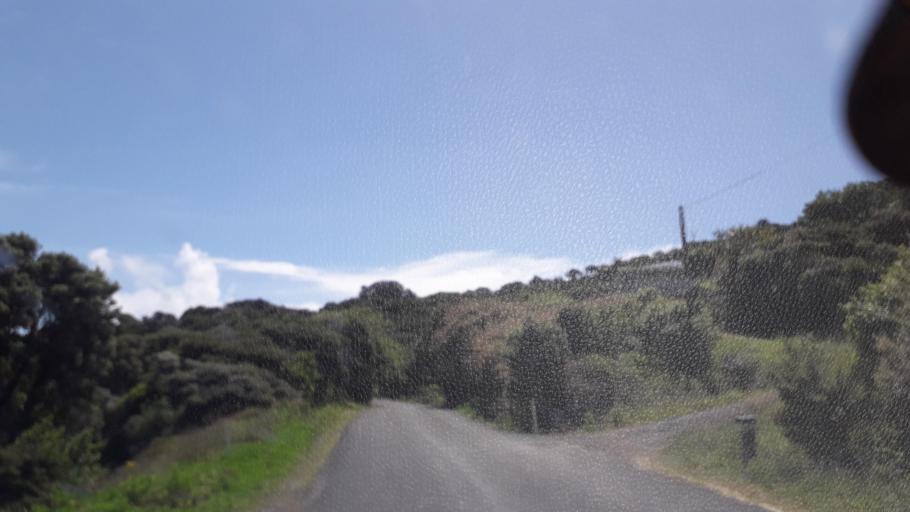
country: NZ
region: Northland
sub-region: Far North District
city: Paihia
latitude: -35.2242
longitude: 174.2616
